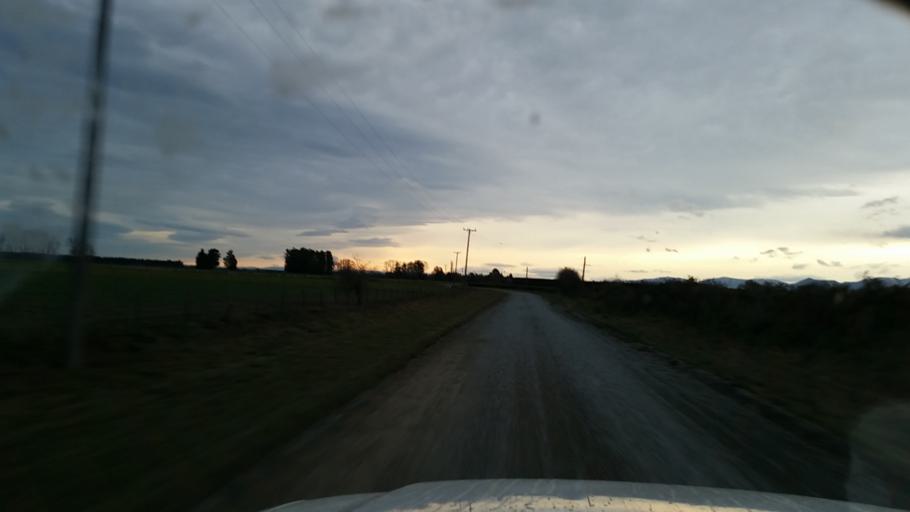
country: NZ
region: Canterbury
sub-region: Ashburton District
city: Ashburton
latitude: -43.8269
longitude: 171.6369
